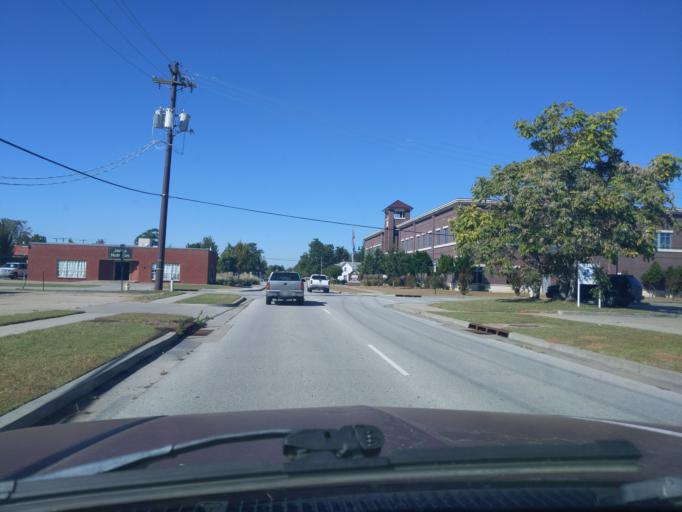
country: US
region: Oklahoma
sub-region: Tulsa County
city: Jenks
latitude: 36.0236
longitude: -95.9666
